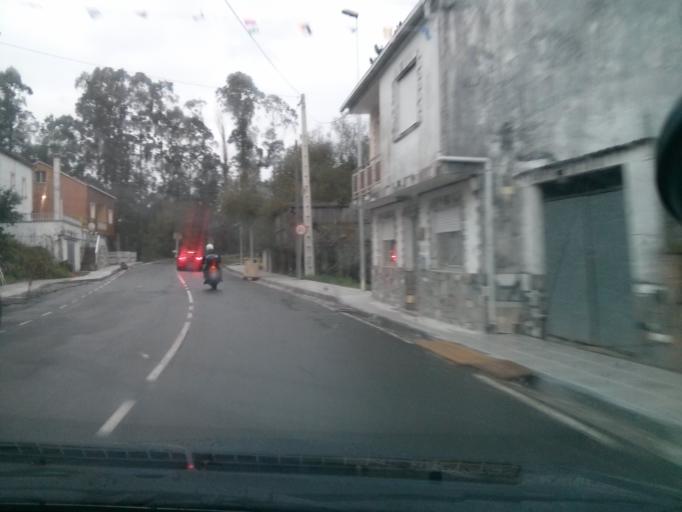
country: ES
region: Galicia
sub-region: Provincia da Coruna
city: Outes
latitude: 42.8338
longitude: -8.8741
